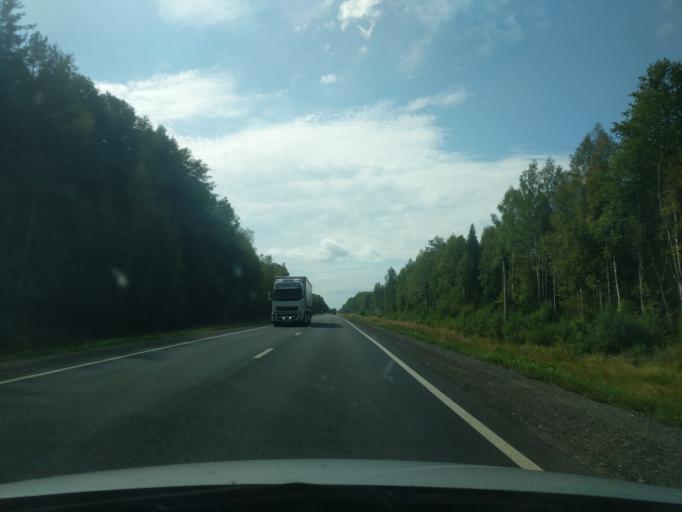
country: RU
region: Kostroma
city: Kadyy
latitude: 57.8184
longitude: 43.2379
